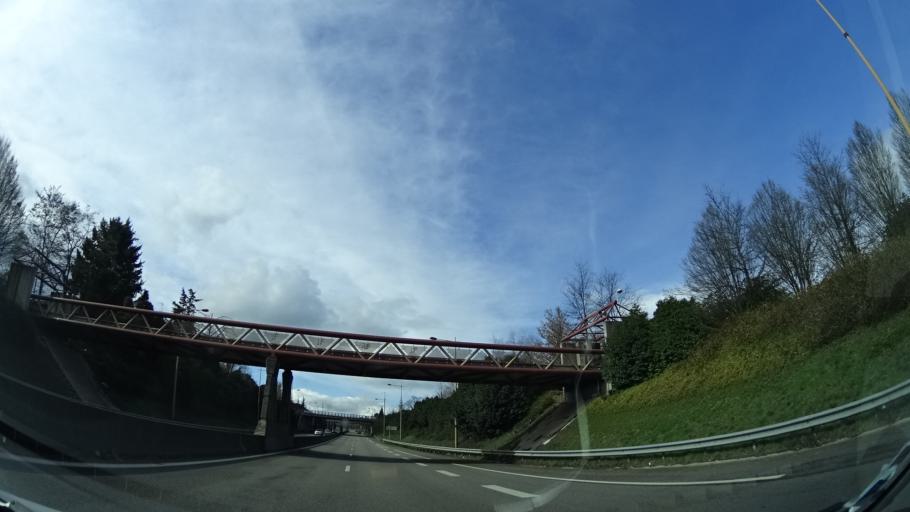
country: FR
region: Rhone-Alpes
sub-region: Departement de la Loire
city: Roanne
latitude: 46.0559
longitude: 4.0758
